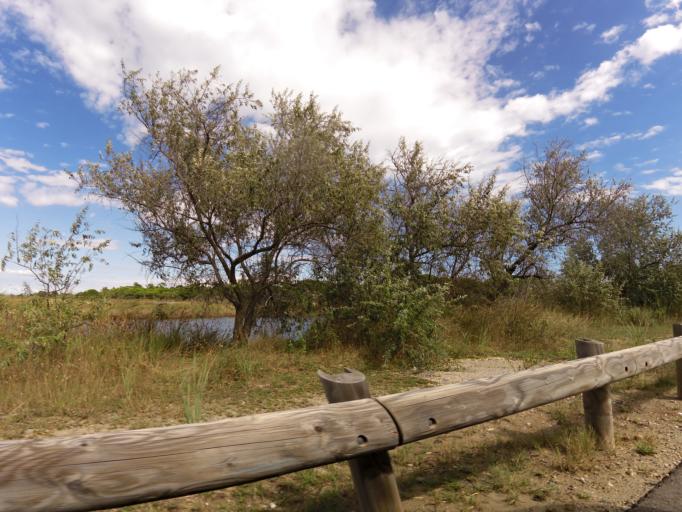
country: FR
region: Languedoc-Roussillon
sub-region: Departement du Gard
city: Le Grau-du-Roi
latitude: 43.4937
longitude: 4.1423
